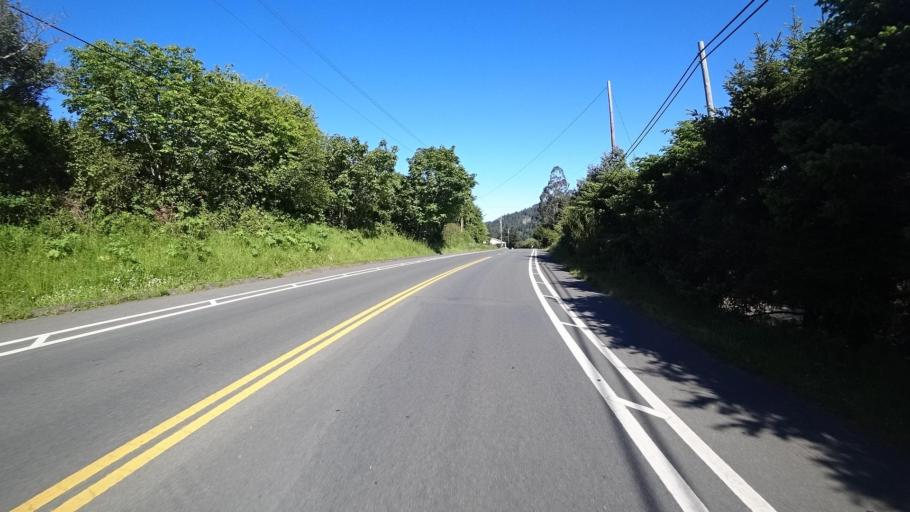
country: US
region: California
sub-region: Humboldt County
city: Rio Dell
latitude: 40.5044
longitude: -124.1107
